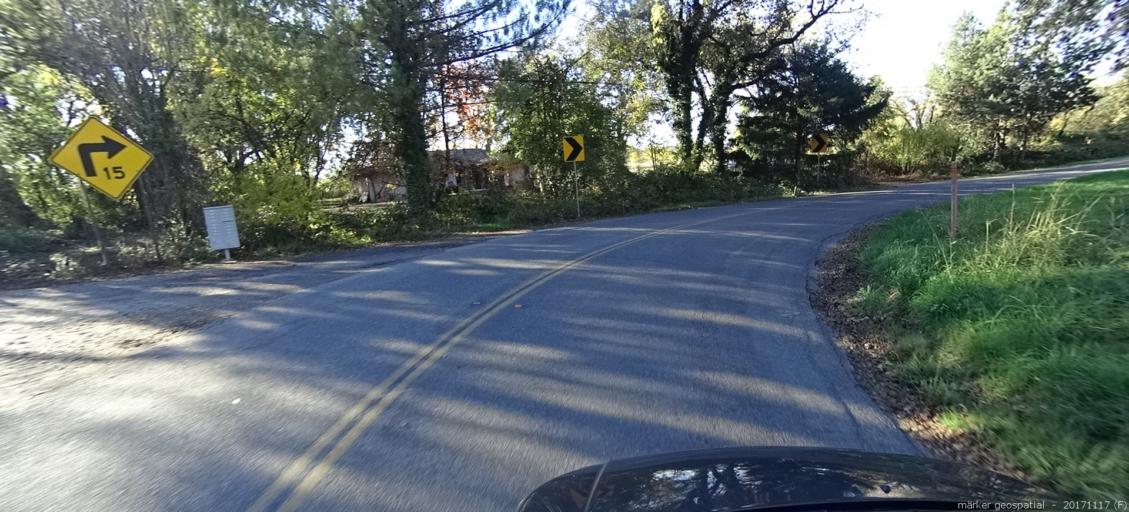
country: US
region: California
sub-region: Shasta County
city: Cottonwood
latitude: 40.3956
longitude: -122.2317
